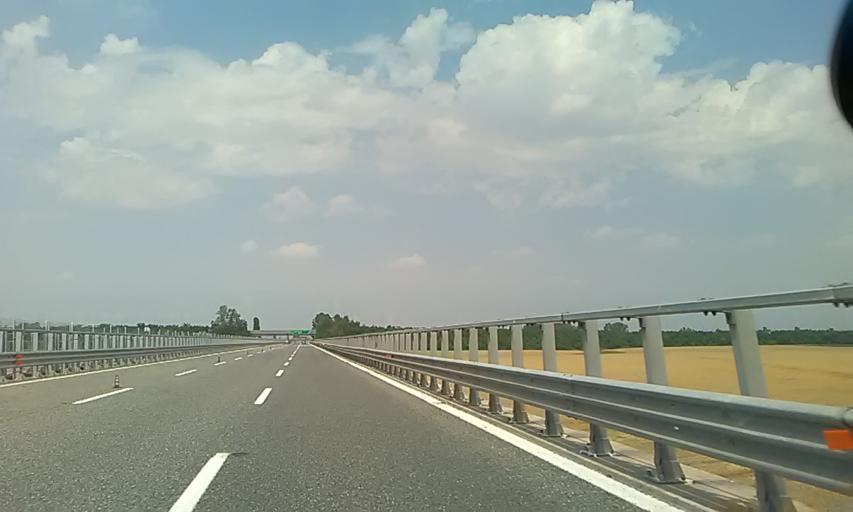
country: IT
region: Piedmont
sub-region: Provincia di Alessandria
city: Castellazzo Bormida
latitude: 44.8663
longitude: 8.5787
